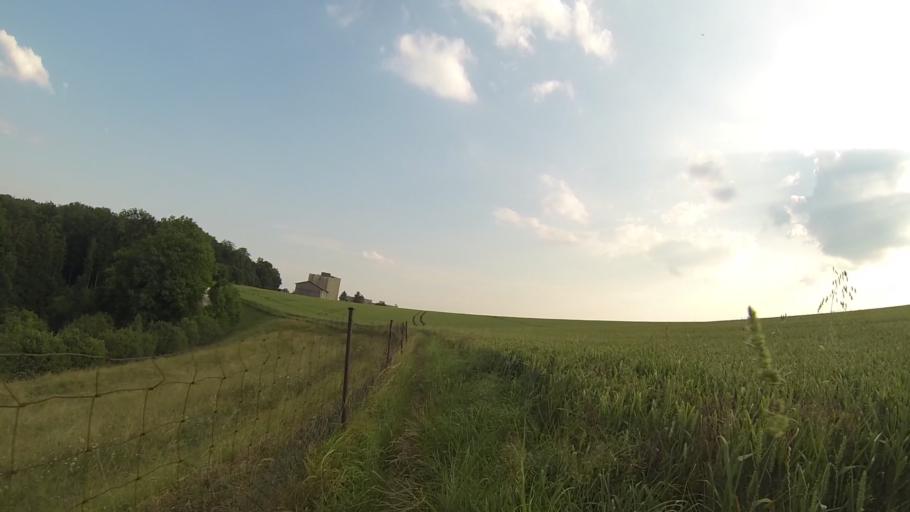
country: DE
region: Baden-Wuerttemberg
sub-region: Tuebingen Region
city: Dornstadt
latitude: 48.4288
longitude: 9.8854
